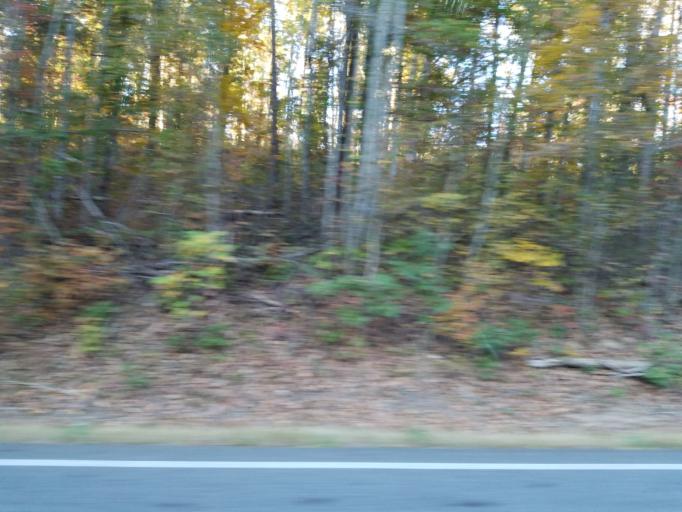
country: US
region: Georgia
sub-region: Pickens County
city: Jasper
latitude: 34.5544
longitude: -84.2935
